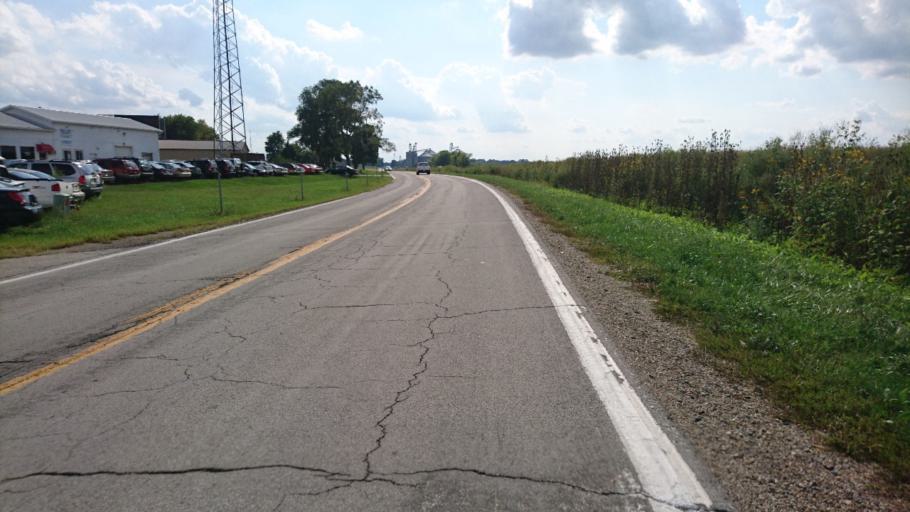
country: US
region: Illinois
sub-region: Logan County
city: Atlanta
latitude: 40.3266
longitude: -89.1554
